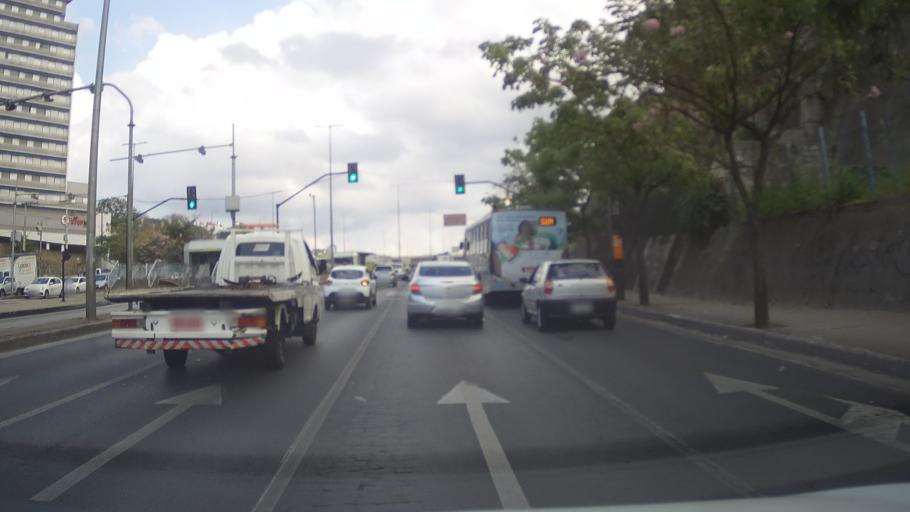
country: BR
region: Minas Gerais
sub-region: Belo Horizonte
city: Belo Horizonte
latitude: -19.8976
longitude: -43.9485
